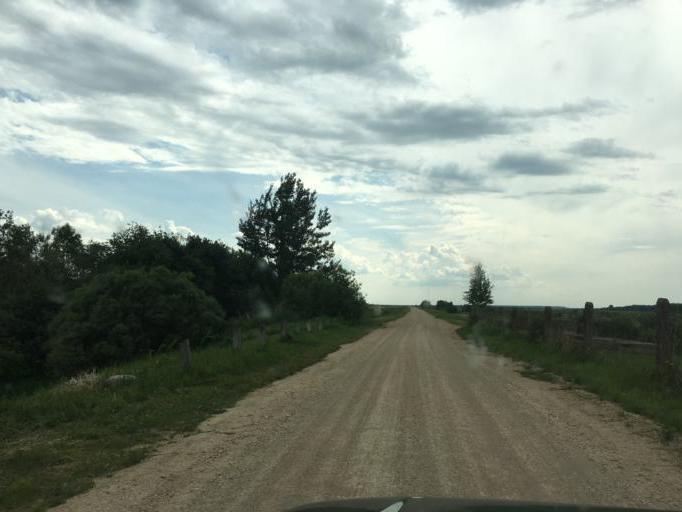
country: LV
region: Lubana
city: Lubana
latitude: 56.8257
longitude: 26.8704
